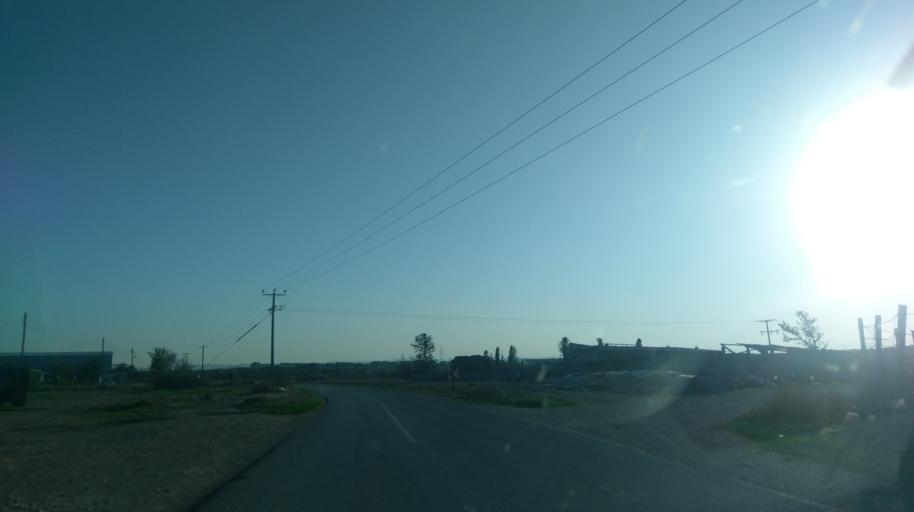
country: CY
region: Ammochostos
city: Lefkonoiko
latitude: 35.2156
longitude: 33.6193
